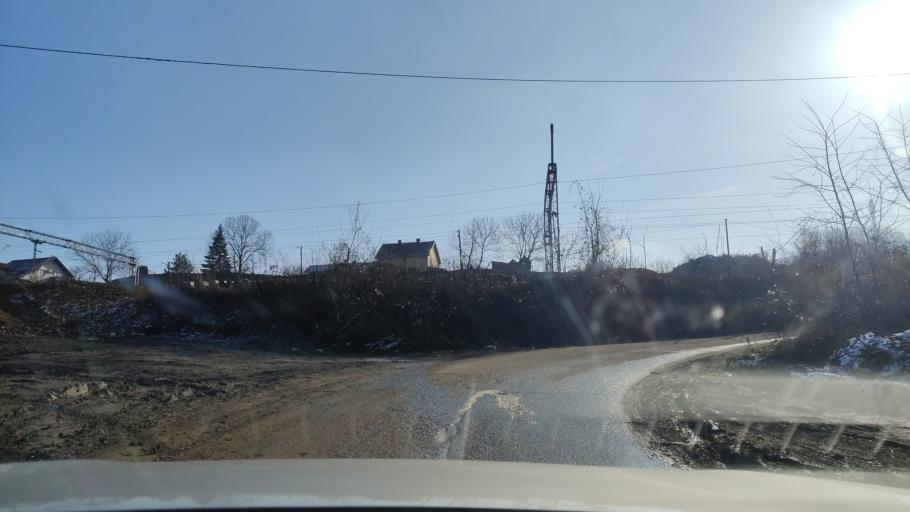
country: RS
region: Central Serbia
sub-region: Belgrade
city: Zvezdara
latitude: 44.7148
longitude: 20.5163
